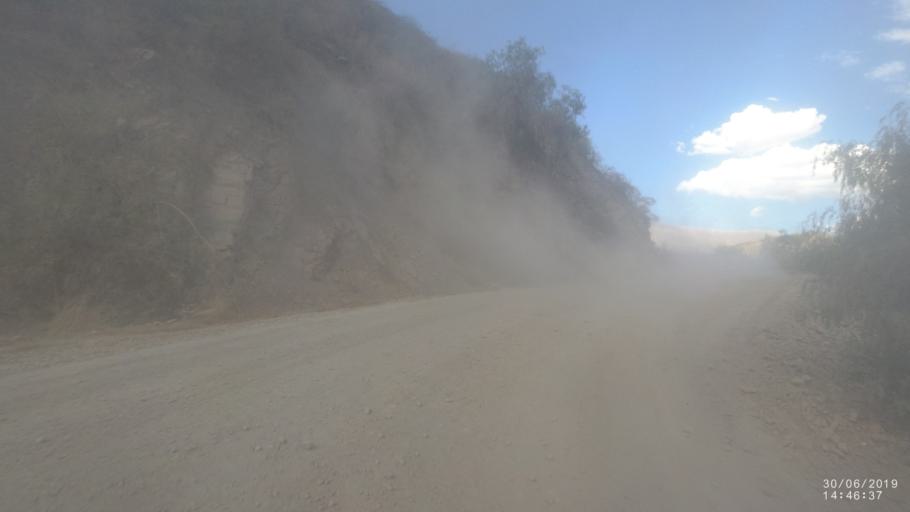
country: BO
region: Cochabamba
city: Irpa Irpa
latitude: -17.7935
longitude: -66.3493
